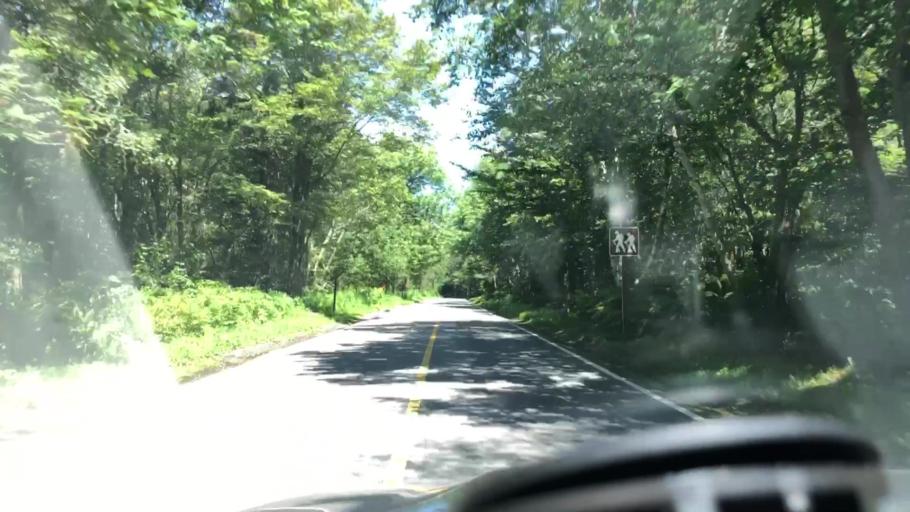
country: US
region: Massachusetts
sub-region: Berkshire County
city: Lanesborough
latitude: 42.5716
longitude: -73.2055
